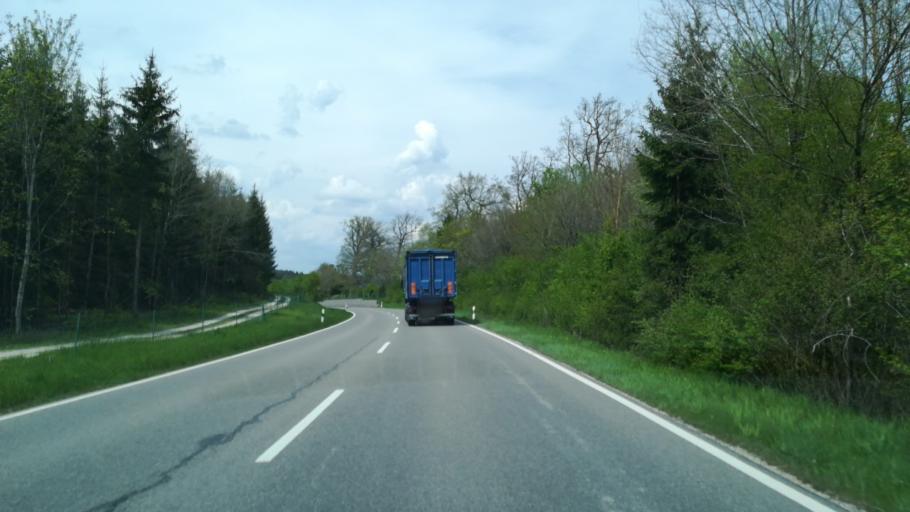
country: DE
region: Baden-Wuerttemberg
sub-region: Tuebingen Region
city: Messkirch
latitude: 47.9790
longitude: 9.0809
